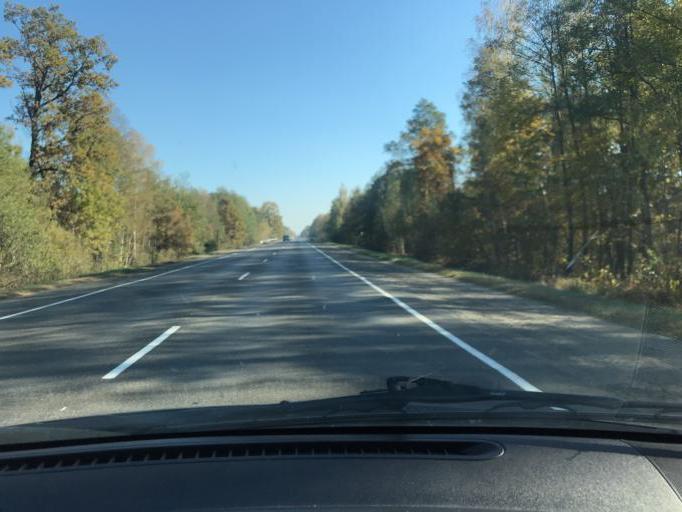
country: BY
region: Brest
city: Mikashevichy
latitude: 52.2419
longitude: 27.4717
